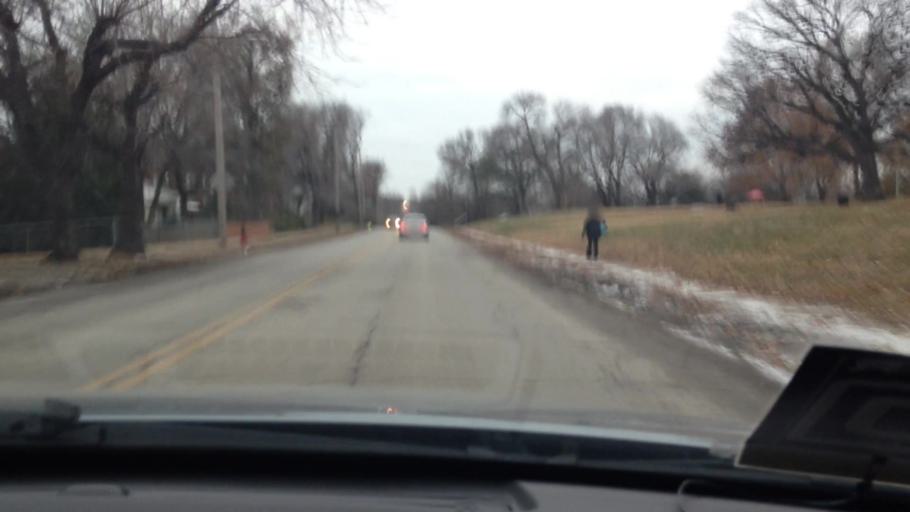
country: US
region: Missouri
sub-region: Clay County
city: North Kansas City
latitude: 39.1120
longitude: -94.5187
